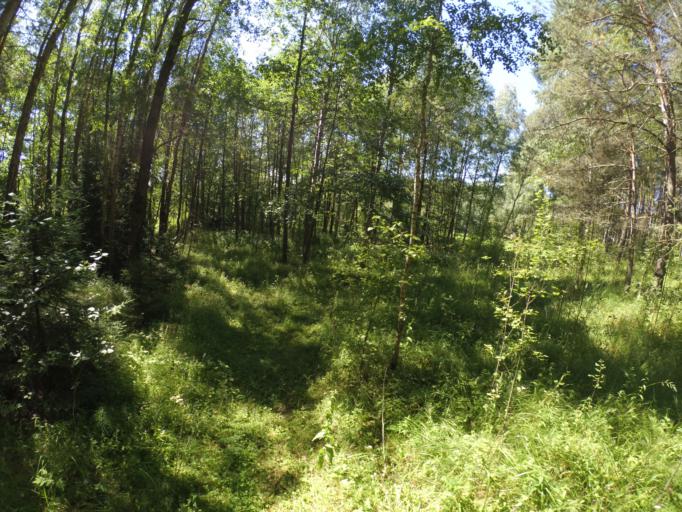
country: RU
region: Moskovskaya
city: Fosforitnyy
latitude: 55.3364
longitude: 38.9231
